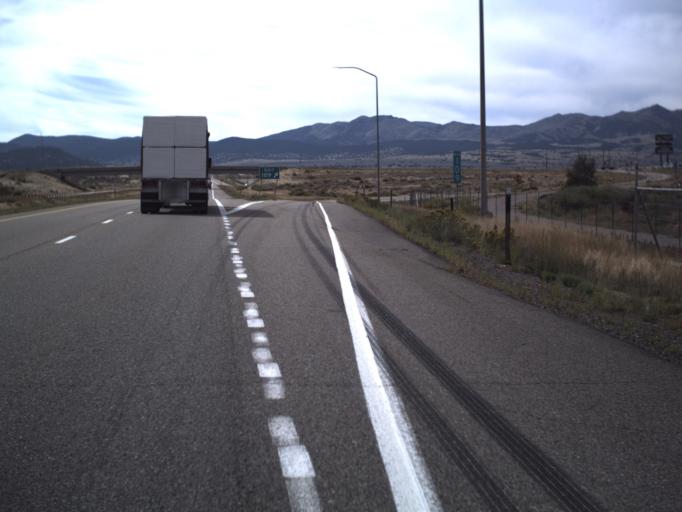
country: US
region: Utah
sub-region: Beaver County
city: Beaver
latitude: 38.2535
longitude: -112.6503
